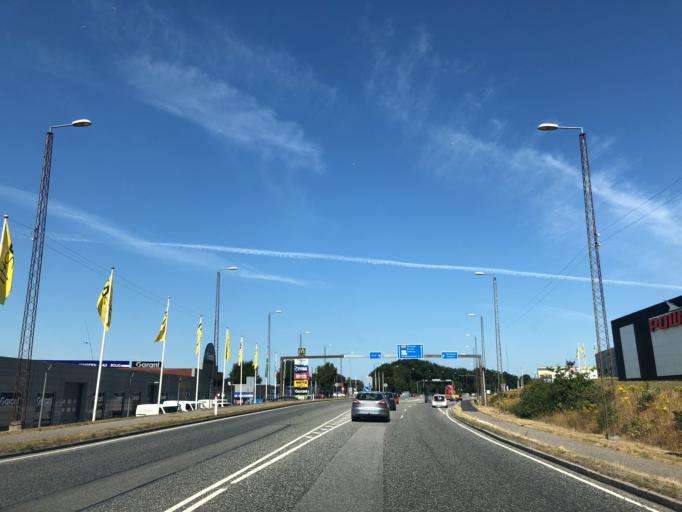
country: DK
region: Central Jutland
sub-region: Holstebro Kommune
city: Holstebro
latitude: 56.3760
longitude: 8.6188
